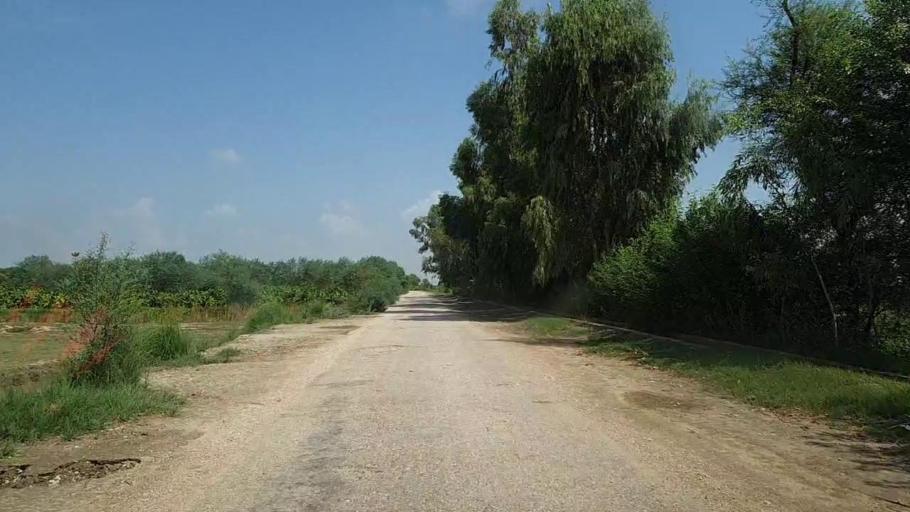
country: PK
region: Sindh
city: Bhiria
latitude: 26.8706
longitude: 68.2553
